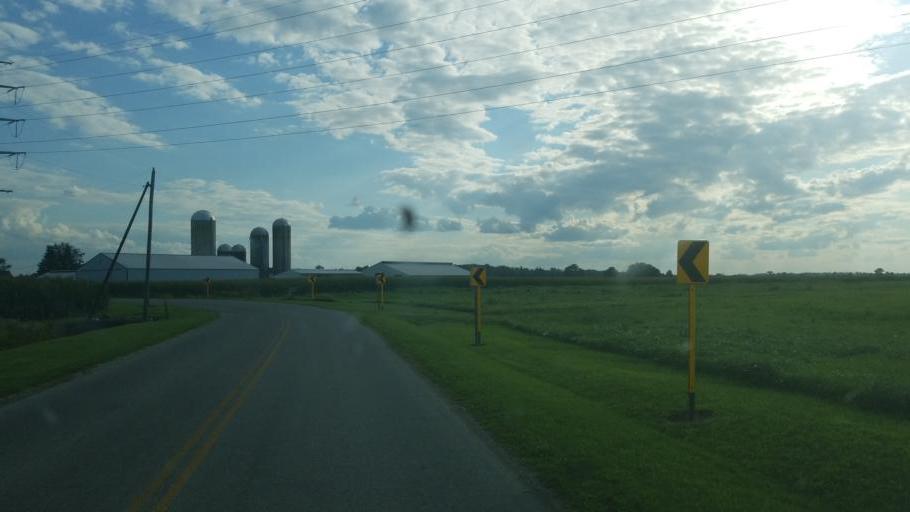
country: US
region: Ohio
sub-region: Seneca County
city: Tiffin
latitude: 41.1555
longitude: -83.1279
